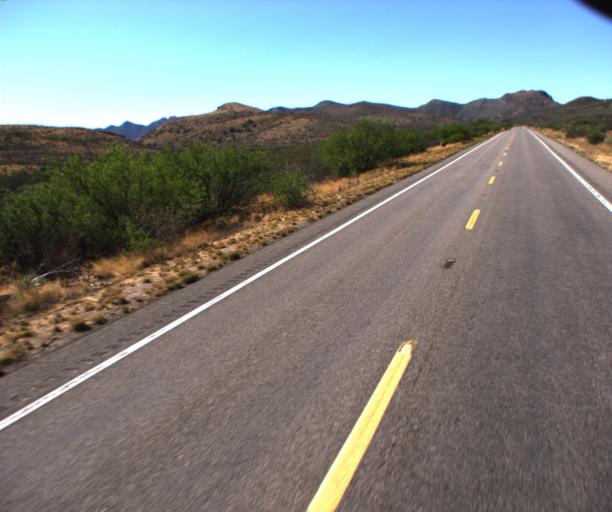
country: US
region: Arizona
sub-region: Cochise County
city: Bisbee
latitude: 31.5329
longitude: -110.0119
